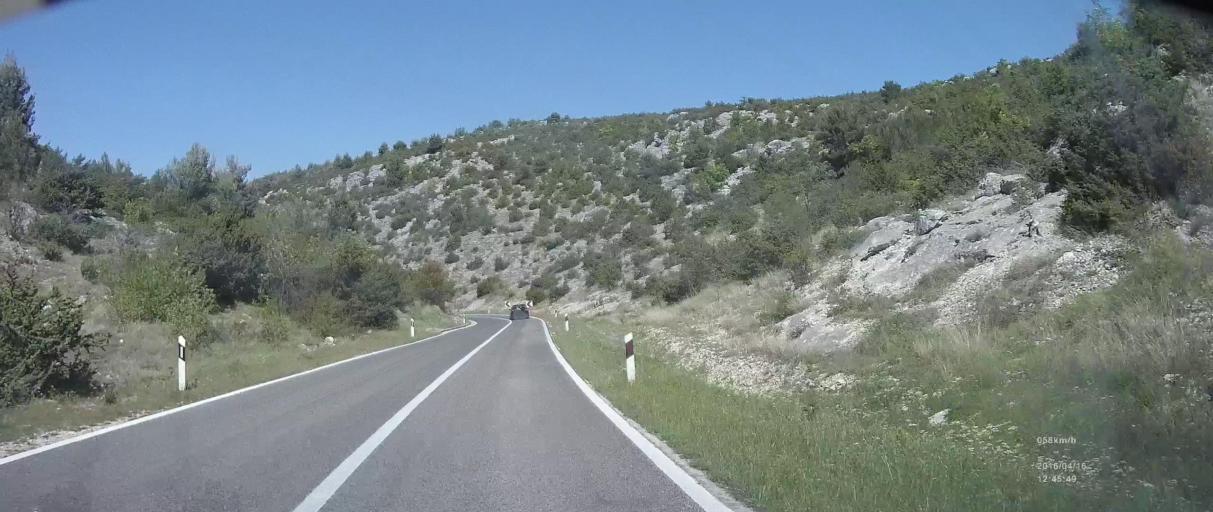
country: HR
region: Sibensko-Kniniska
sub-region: Grad Sibenik
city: Brodarica
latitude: 43.6512
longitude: 16.0600
